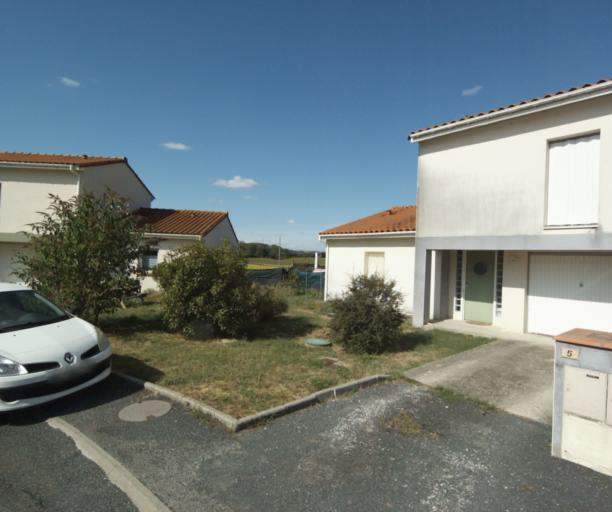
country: FR
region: Midi-Pyrenees
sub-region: Departement du Tarn
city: Puylaurens
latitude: 43.5217
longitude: 1.9857
